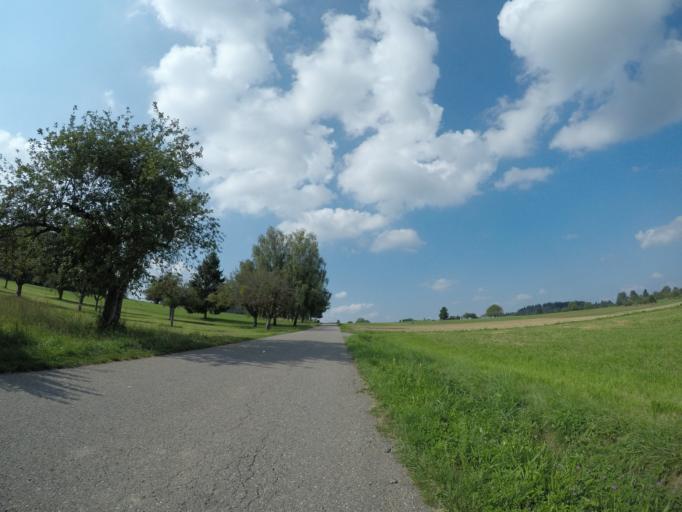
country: DE
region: Baden-Wuerttemberg
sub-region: Tuebingen Region
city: Pfullingen
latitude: 48.4571
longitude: 9.1951
